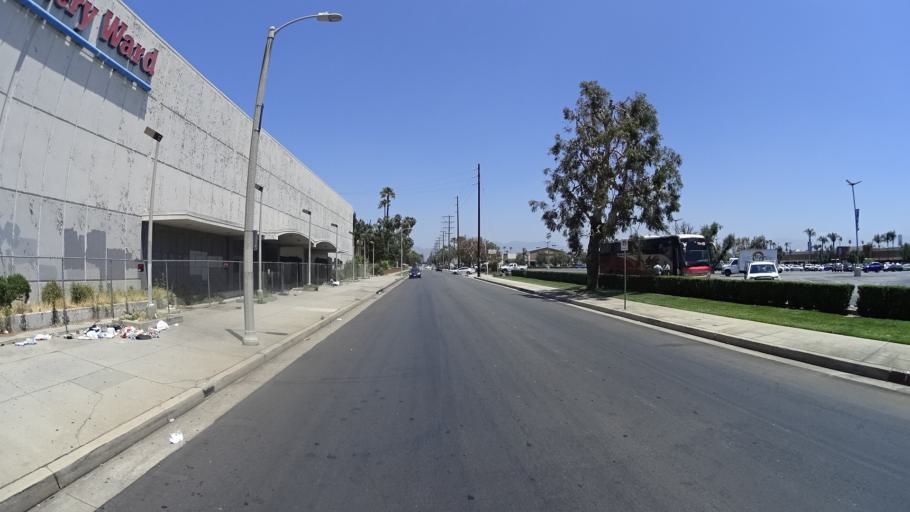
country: US
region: California
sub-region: Los Angeles County
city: Van Nuys
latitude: 34.2233
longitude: -118.4516
